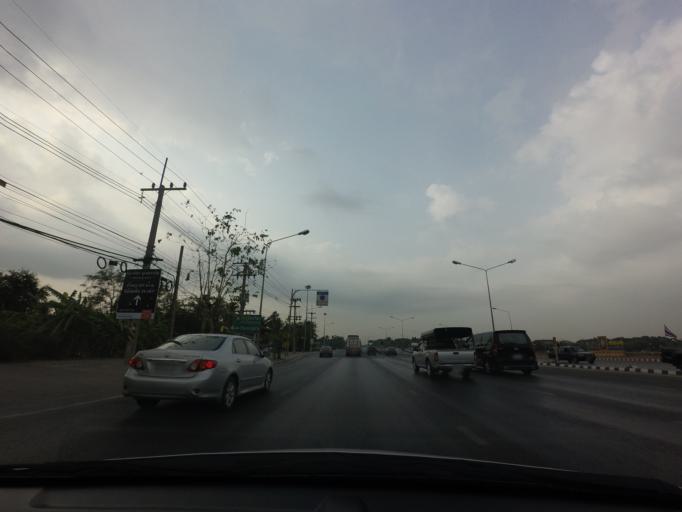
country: TH
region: Bangkok
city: Thawi Watthana
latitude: 13.7785
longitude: 100.3281
